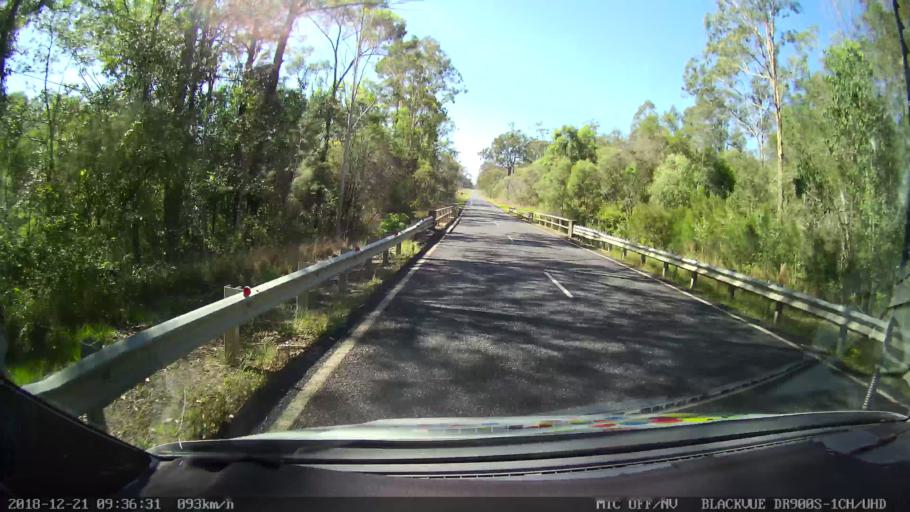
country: AU
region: New South Wales
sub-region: Clarence Valley
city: Grafton
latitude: -29.5243
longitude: 152.9835
